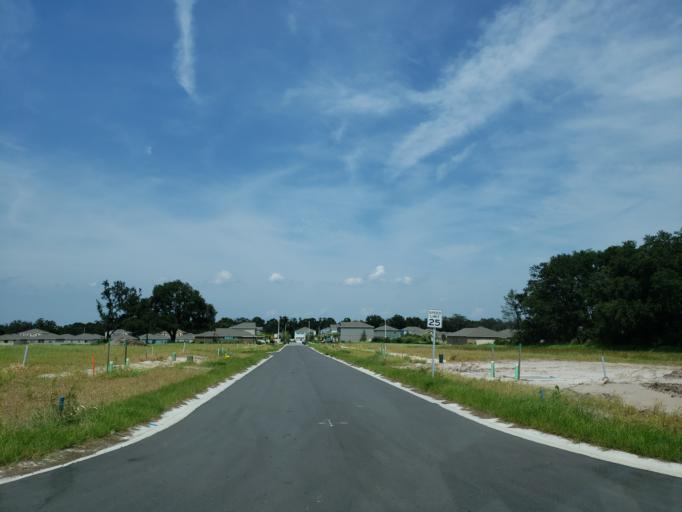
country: US
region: Florida
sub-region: Hillsborough County
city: Riverview
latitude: 27.8468
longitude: -82.3374
